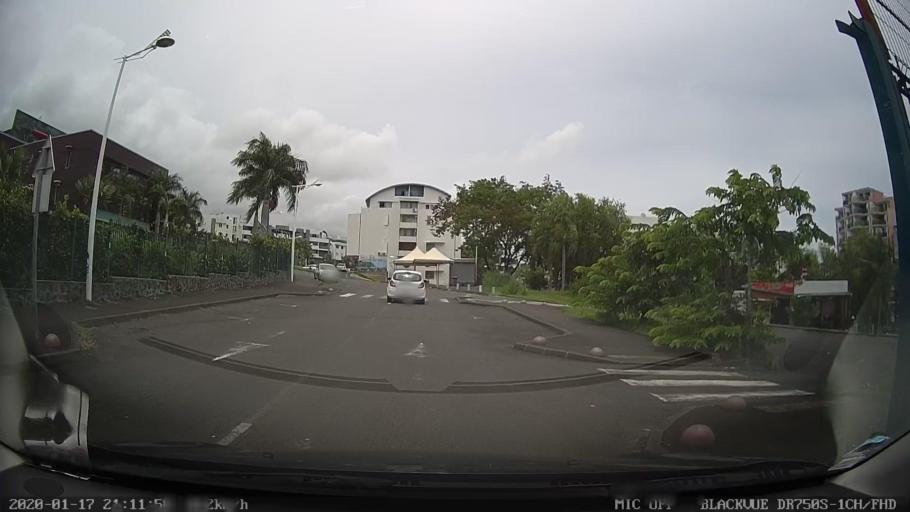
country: RE
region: Reunion
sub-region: Reunion
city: Saint-Denis
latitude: -20.9022
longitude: 55.4821
